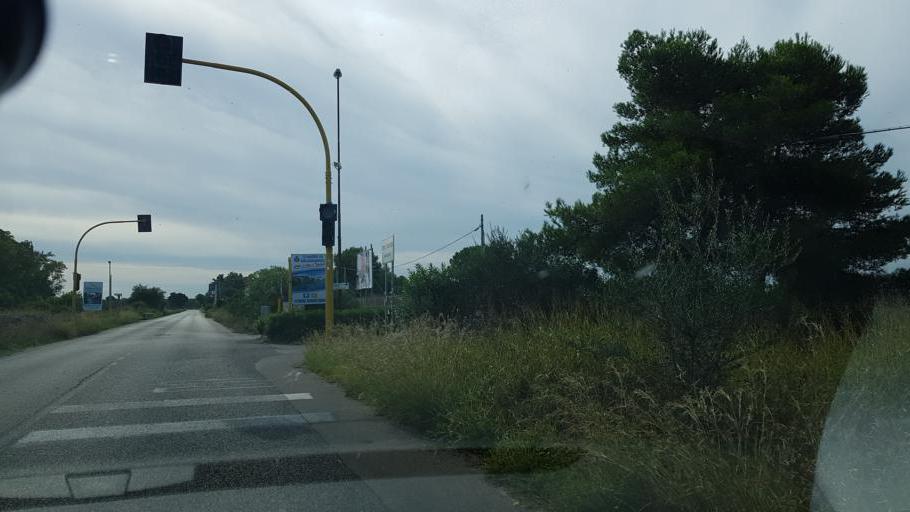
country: IT
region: Apulia
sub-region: Provincia di Lecce
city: Borgagne
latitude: 40.2588
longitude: 18.4357
